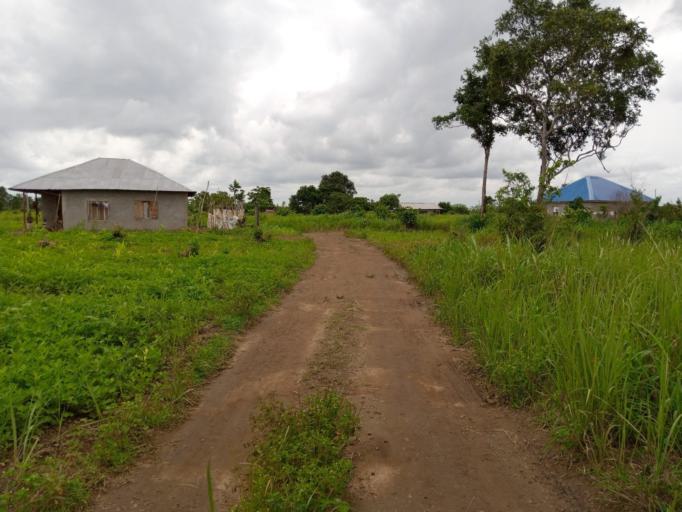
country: SL
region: Southern Province
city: Moyamba
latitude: 8.1692
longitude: -12.4180
